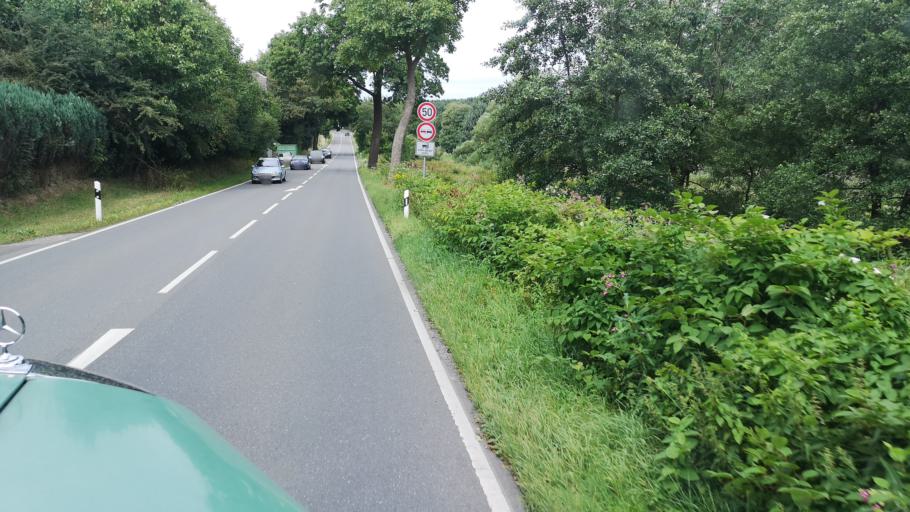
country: DE
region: North Rhine-Westphalia
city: Huckeswagen
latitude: 51.1481
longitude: 7.2950
